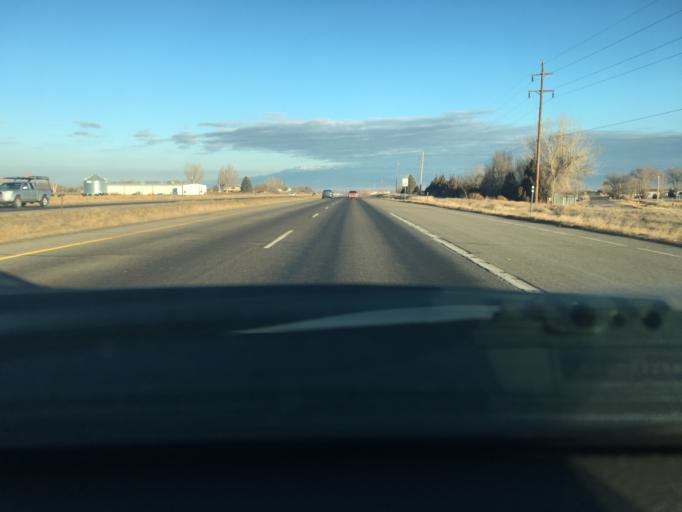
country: US
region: Colorado
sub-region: Montrose County
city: Olathe
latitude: 38.5770
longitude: -107.9627
